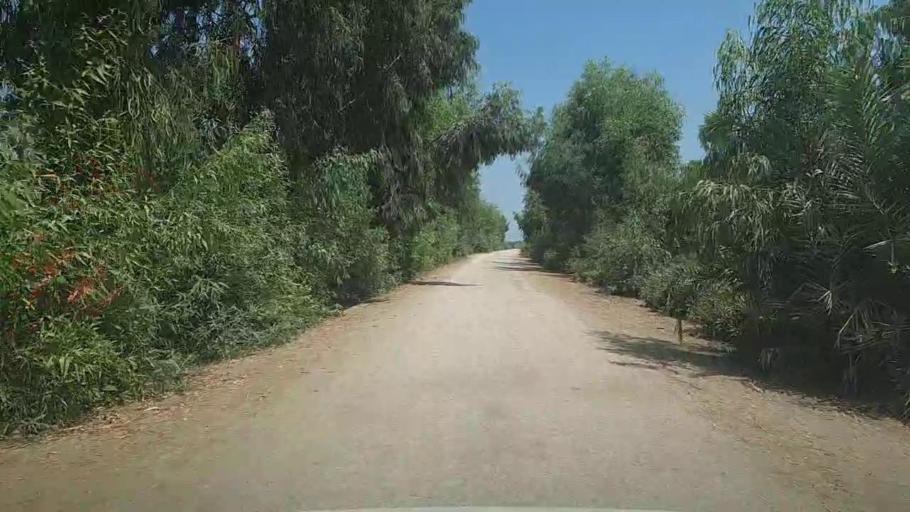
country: PK
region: Sindh
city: Kandhkot
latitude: 28.2695
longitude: 69.2148
